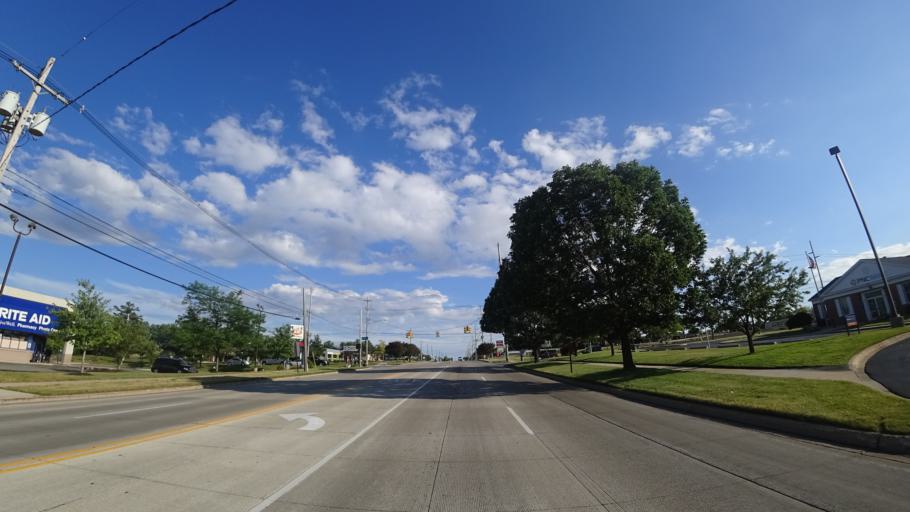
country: US
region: Michigan
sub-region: Ottawa County
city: Holland
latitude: 42.7623
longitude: -86.1167
